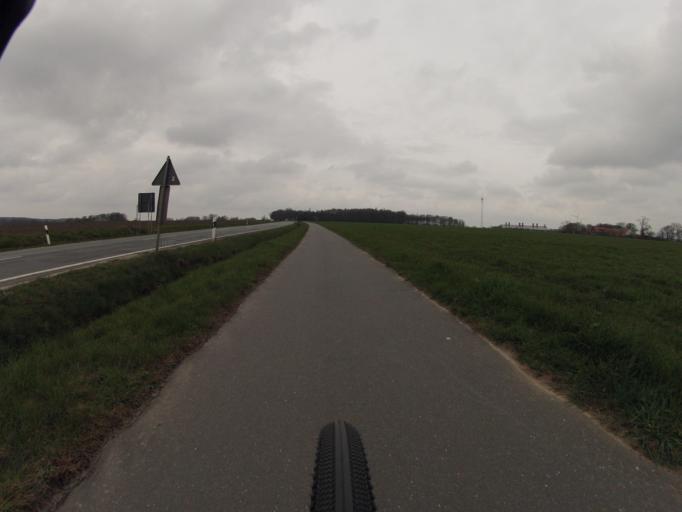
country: DE
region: North Rhine-Westphalia
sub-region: Regierungsbezirk Munster
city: Mettingen
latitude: 52.3322
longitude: 7.7484
